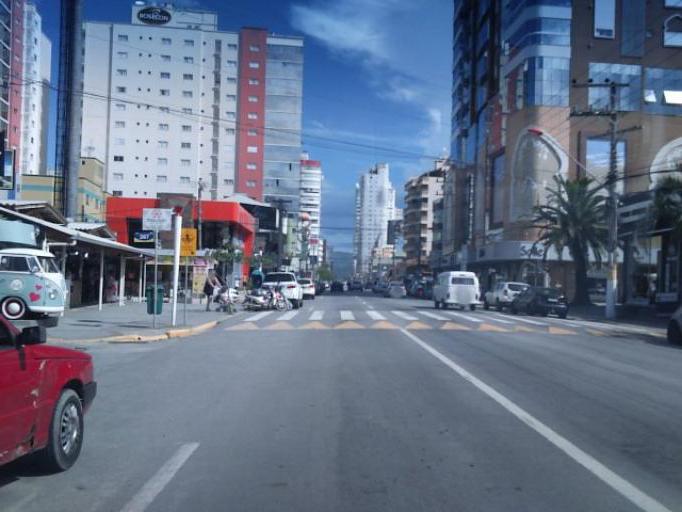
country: BR
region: Santa Catarina
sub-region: Itapema
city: Itapema
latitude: -27.1342
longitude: -48.5977
